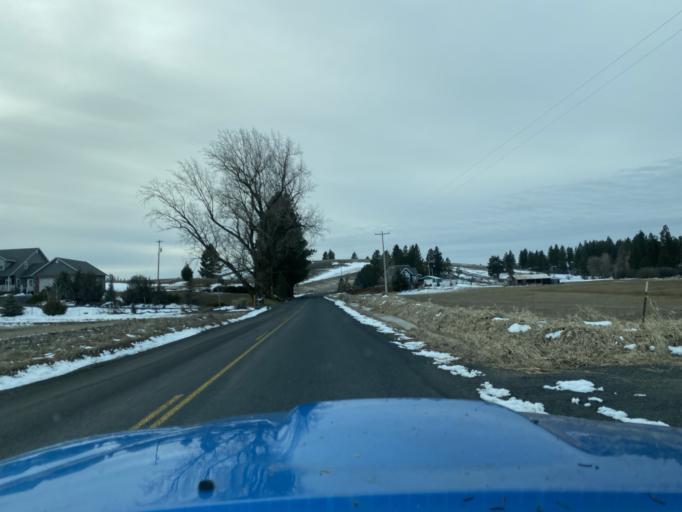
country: US
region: Idaho
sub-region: Latah County
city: Moscow
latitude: 46.6869
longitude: -116.9035
